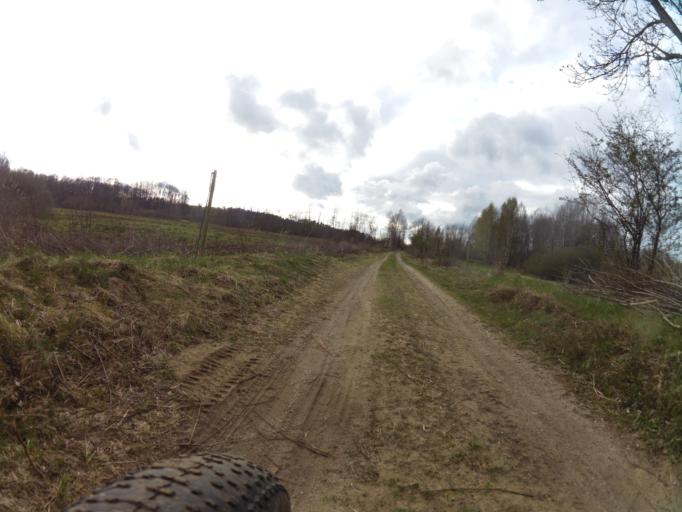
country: PL
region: West Pomeranian Voivodeship
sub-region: Powiat slawienski
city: Slawno
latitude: 54.3314
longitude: 16.7255
